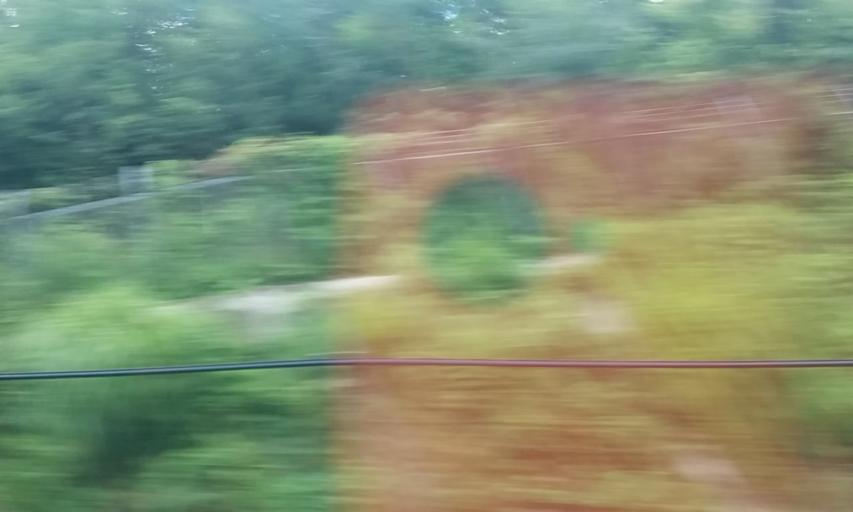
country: JP
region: Fukushima
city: Sukagawa
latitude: 37.2503
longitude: 140.3022
